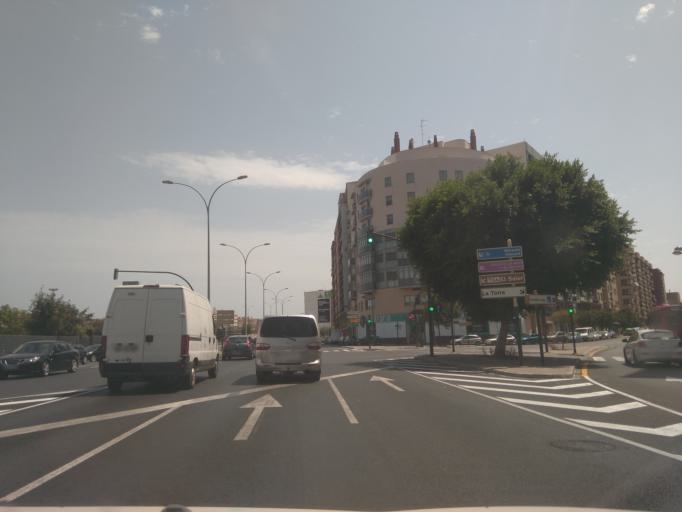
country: ES
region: Valencia
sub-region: Provincia de Valencia
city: Valencia
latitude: 39.4578
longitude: -0.3836
